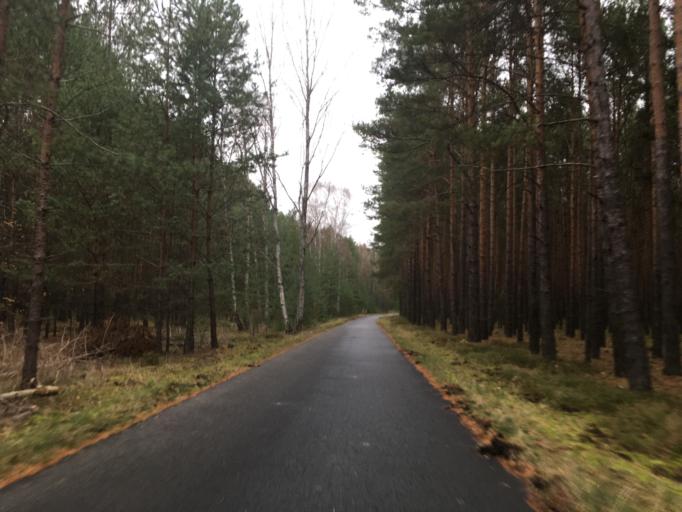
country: DE
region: Brandenburg
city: Mullrose
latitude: 52.2321
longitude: 14.4472
